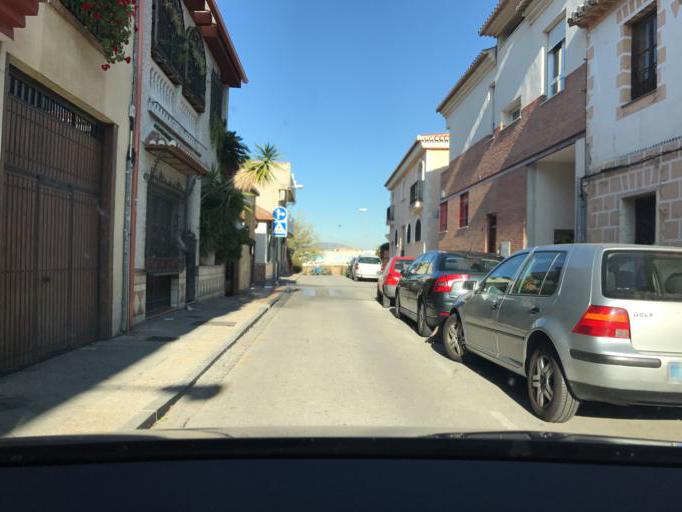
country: ES
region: Andalusia
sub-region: Provincia de Granada
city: Maracena
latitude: 37.2013
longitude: -3.6279
